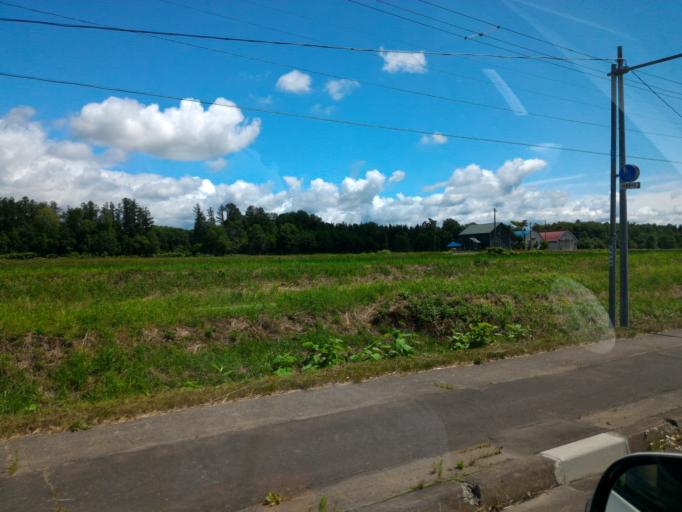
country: JP
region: Hokkaido
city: Nayoro
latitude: 44.5084
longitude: 142.3337
